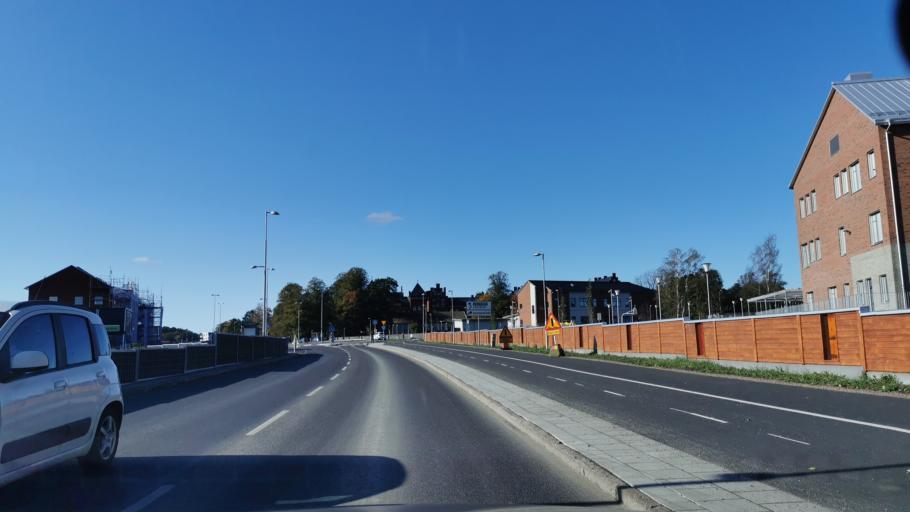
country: SE
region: Vaestra Goetaland
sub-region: Goteborg
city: Eriksbo
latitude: 57.7349
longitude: 12.0381
